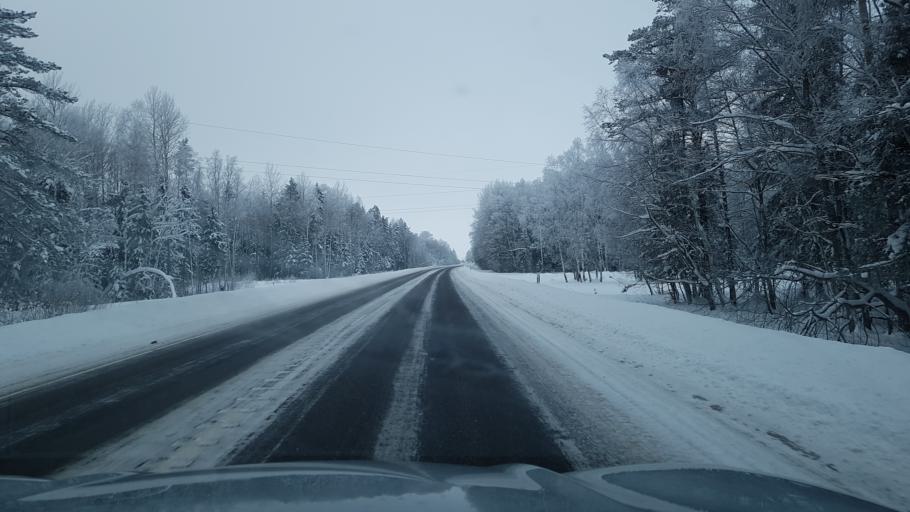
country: EE
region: Ida-Virumaa
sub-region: Johvi vald
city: Johvi
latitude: 59.3040
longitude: 27.3943
